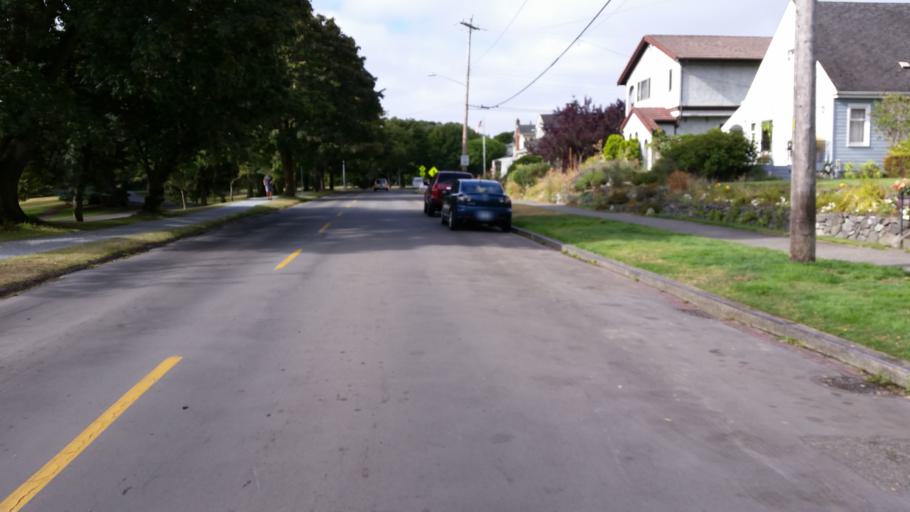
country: US
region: Washington
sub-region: King County
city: Shoreline
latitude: 47.6841
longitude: -122.3397
